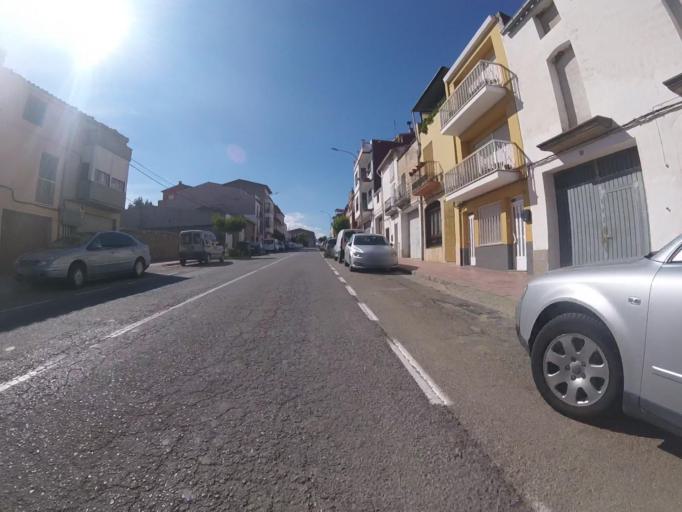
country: ES
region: Valencia
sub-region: Provincia de Castello
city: Albocasser
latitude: 40.3554
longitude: 0.0230
